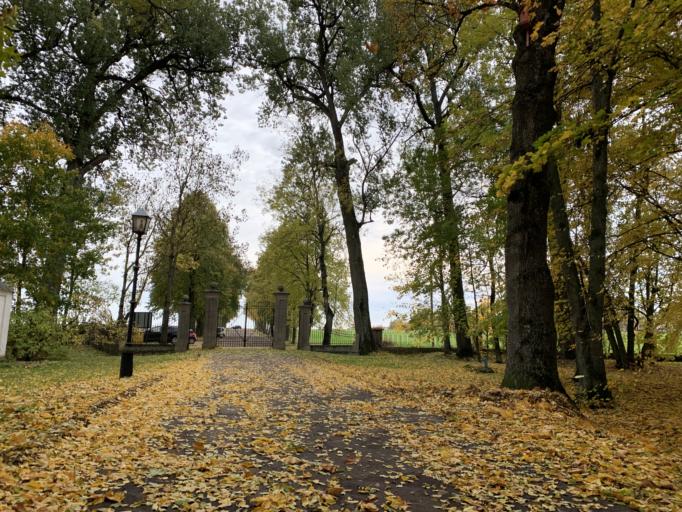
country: BY
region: Minsk
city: Nyasvizh
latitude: 53.2215
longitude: 26.7014
